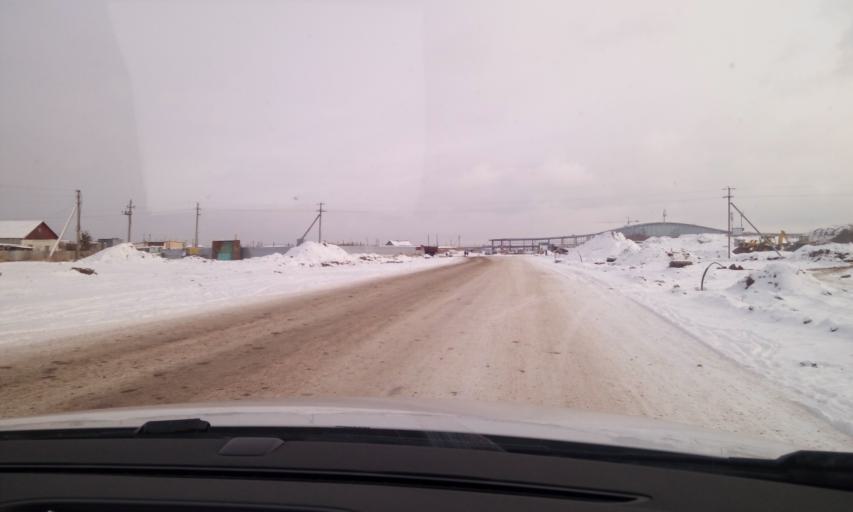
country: KZ
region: Astana Qalasy
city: Astana
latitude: 51.1177
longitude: 71.5135
